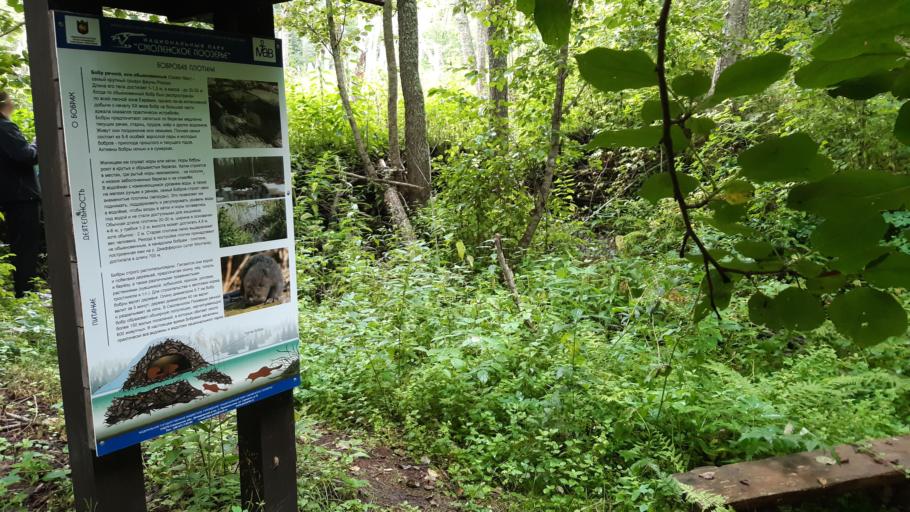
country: RU
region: Smolensk
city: Demidov
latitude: 55.4860
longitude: 31.8168
